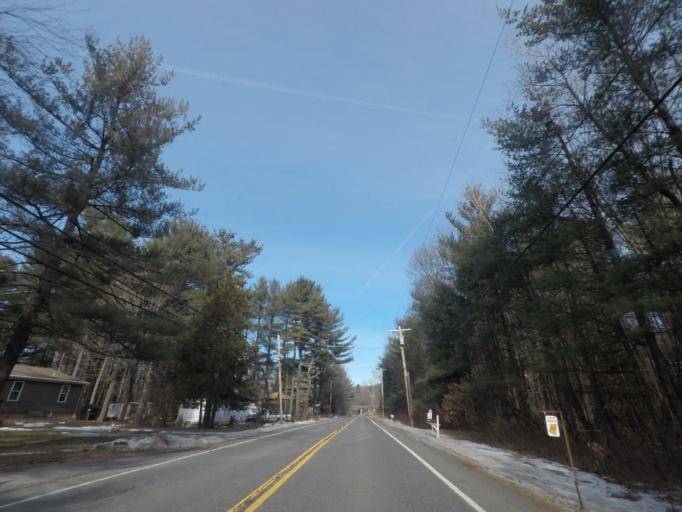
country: US
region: New York
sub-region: Rensselaer County
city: Nassau
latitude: 42.4782
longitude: -73.6273
